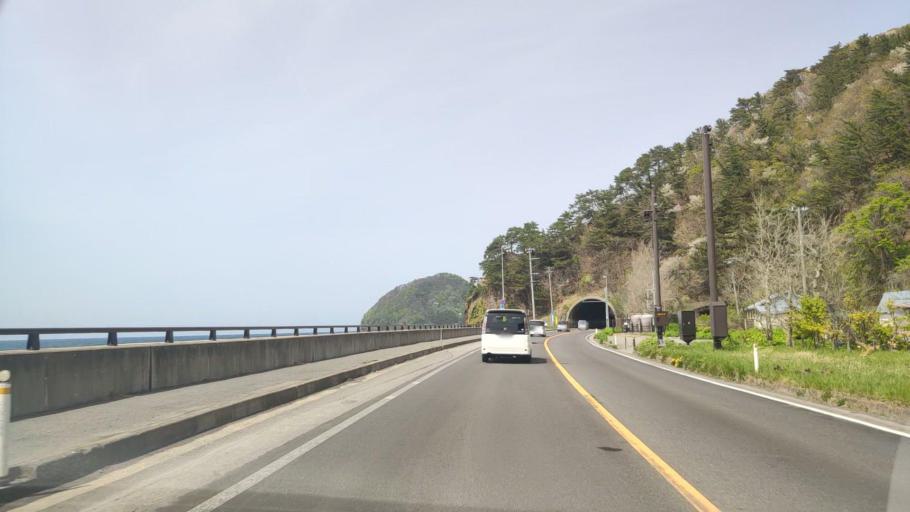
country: JP
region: Aomori
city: Aomori Shi
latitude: 40.8814
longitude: 140.8501
